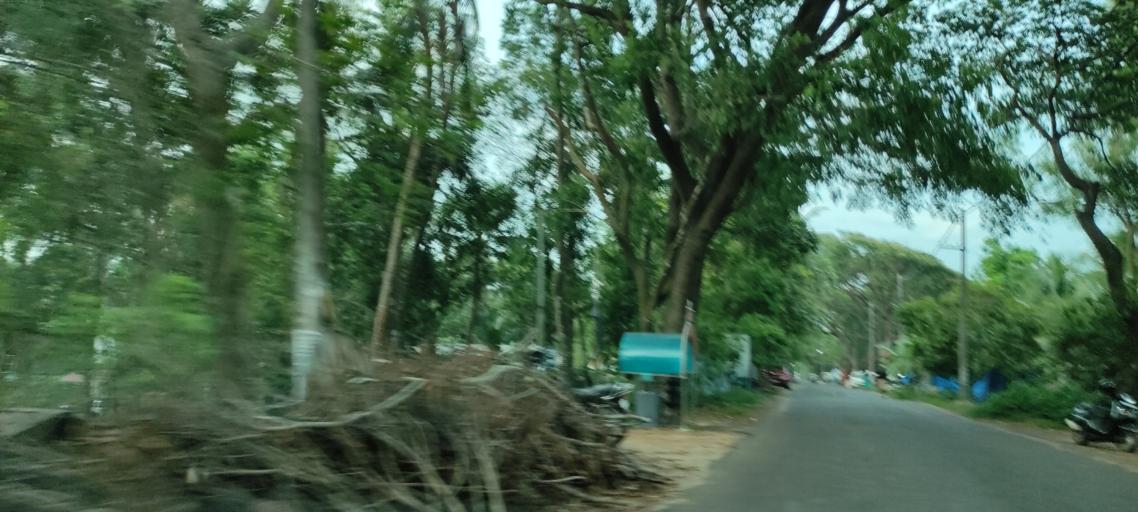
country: IN
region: Kerala
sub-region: Alappuzha
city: Shertallai
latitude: 9.7000
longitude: 76.3559
